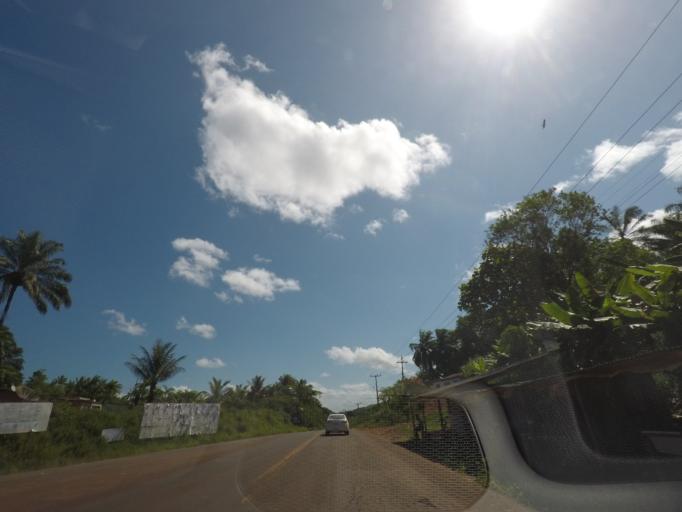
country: BR
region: Bahia
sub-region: Itubera
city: Itubera
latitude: -13.6728
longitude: -39.1231
